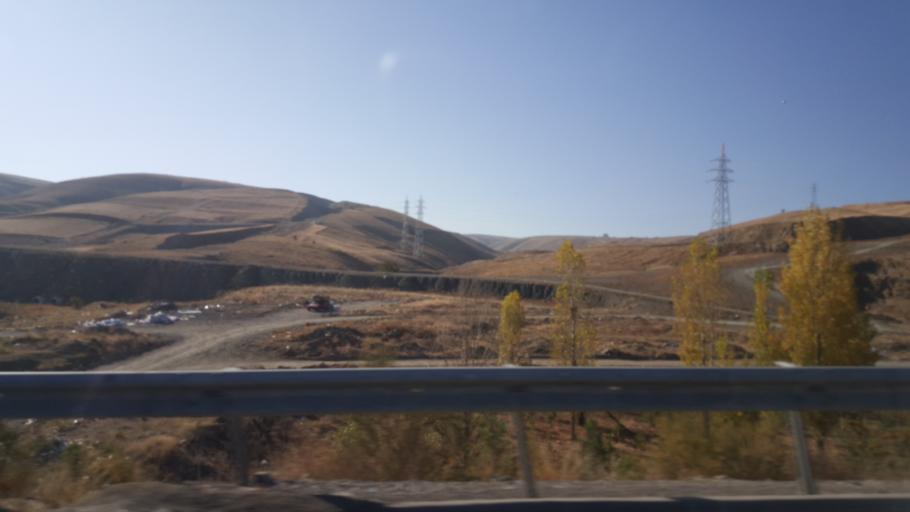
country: TR
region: Ankara
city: Mamak
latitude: 39.8716
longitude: 32.9166
